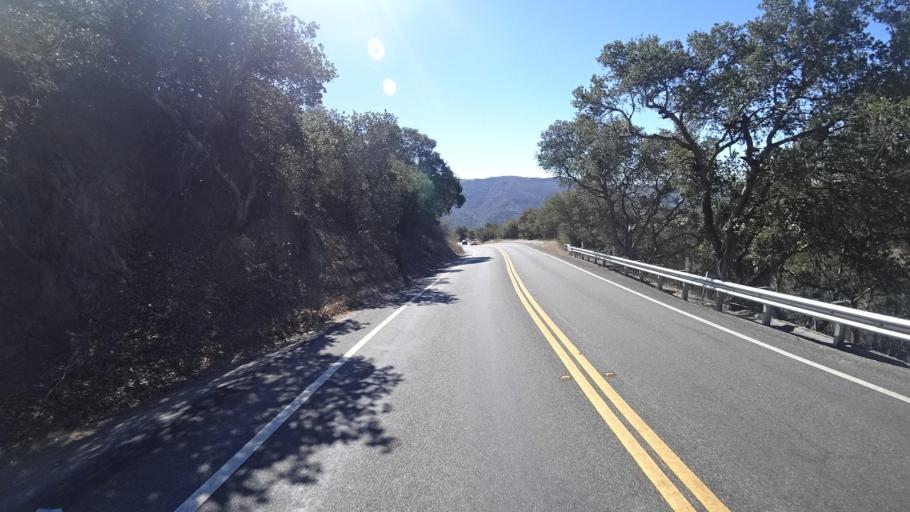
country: US
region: California
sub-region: Monterey County
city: Carmel Valley Village
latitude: 36.5235
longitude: -121.7551
